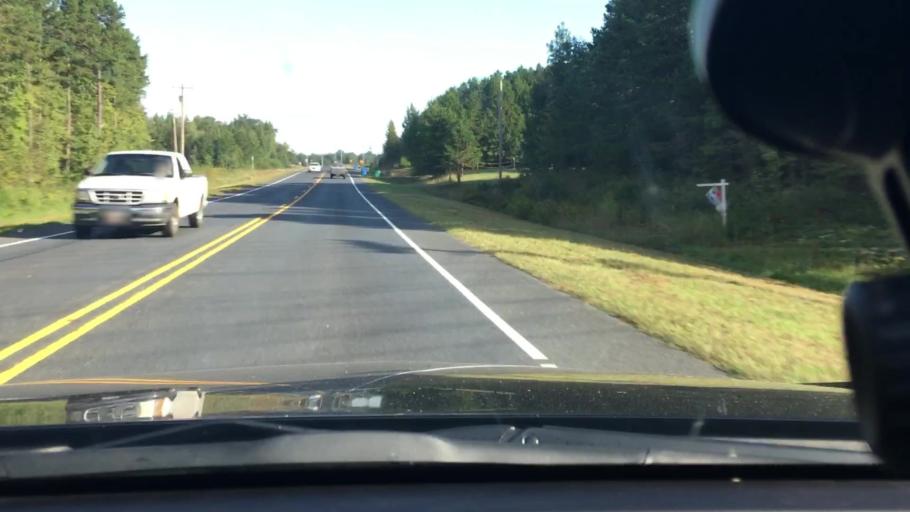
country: US
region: North Carolina
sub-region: Stanly County
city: Albemarle
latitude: 35.3721
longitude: -80.1699
